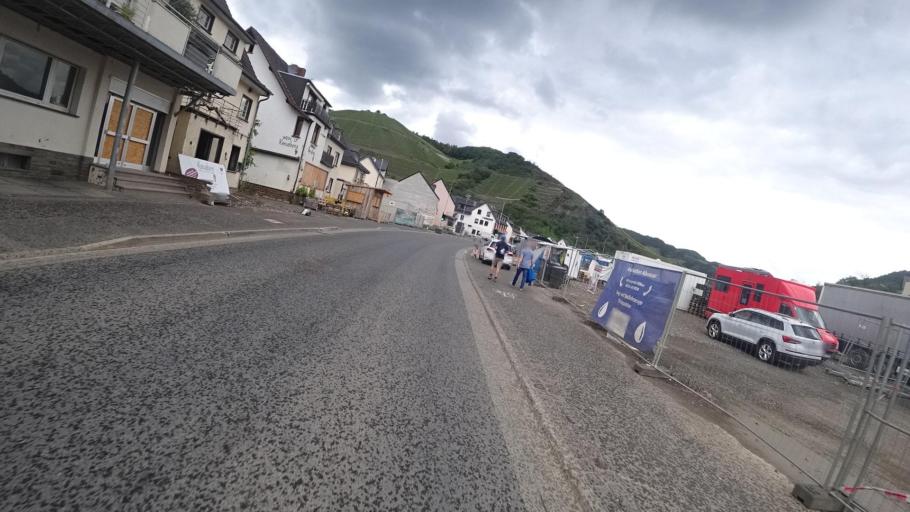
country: DE
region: Rheinland-Pfalz
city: Dernau
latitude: 50.5340
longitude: 7.0453
